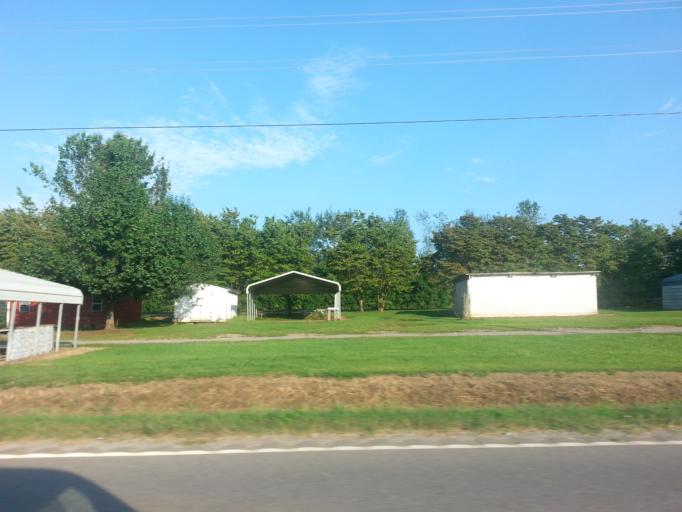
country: US
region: Tennessee
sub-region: Monroe County
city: Sweetwater
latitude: 35.5482
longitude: -84.5165
